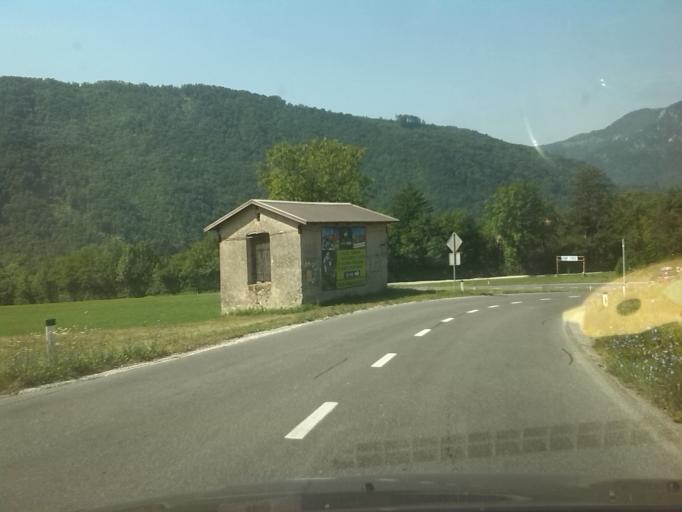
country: SI
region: Tolmin
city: Tolmin
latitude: 46.1808
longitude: 13.7404
